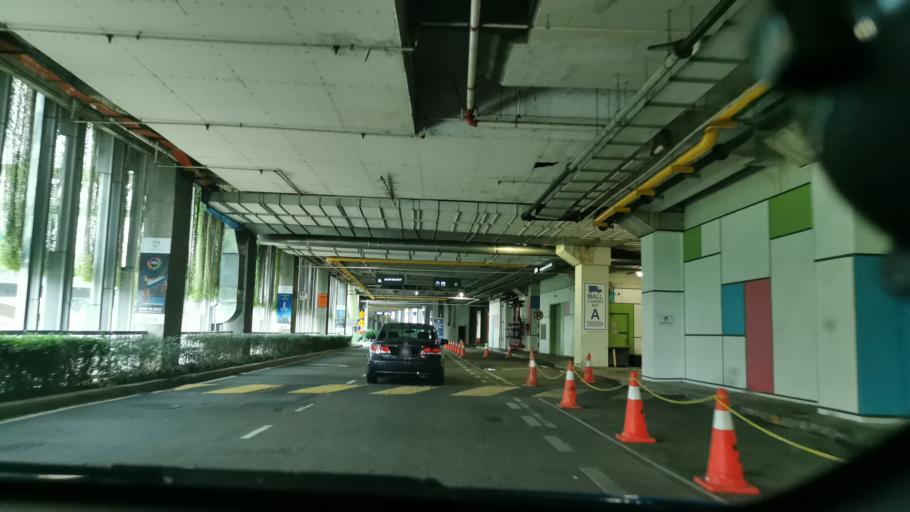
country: MY
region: Kuala Lumpur
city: Kuala Lumpur
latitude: 3.1193
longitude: 101.6745
